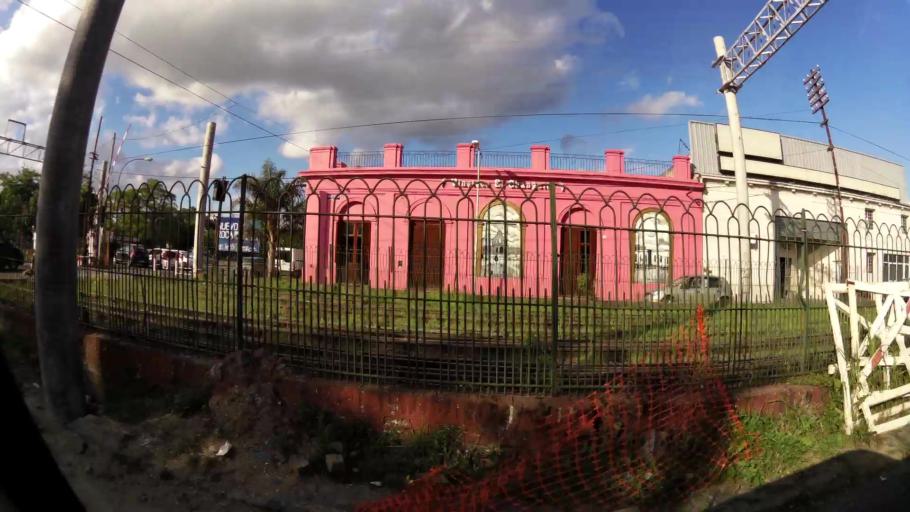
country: AR
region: Buenos Aires
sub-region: Partido de La Plata
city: La Plata
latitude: -34.8919
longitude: -57.9669
